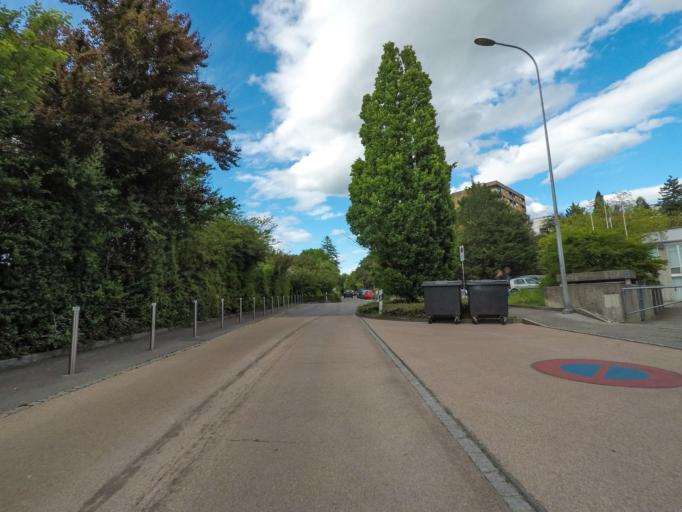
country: CH
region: Geneva
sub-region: Geneva
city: Meyrin
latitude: 46.2388
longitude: 6.0765
